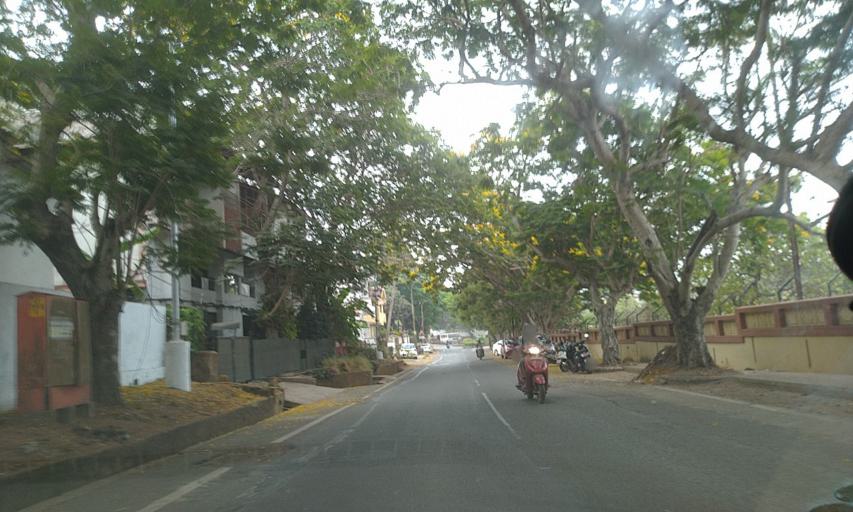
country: IN
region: Goa
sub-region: North Goa
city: Panaji
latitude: 15.4888
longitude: 73.8259
